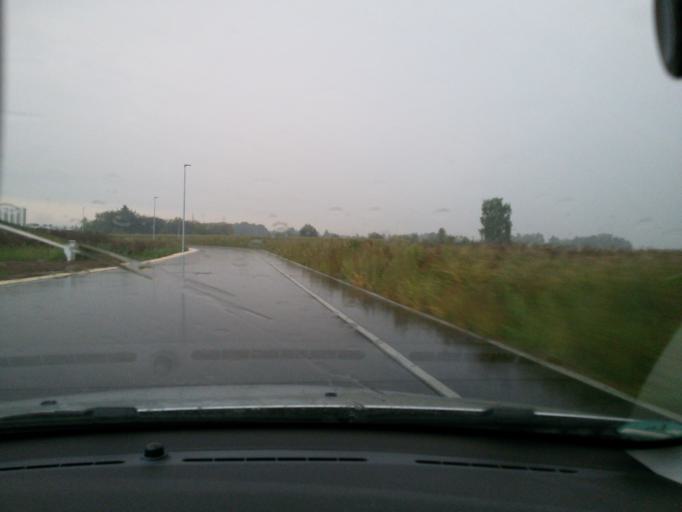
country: DE
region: Bavaria
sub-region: Swabia
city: Langerringen
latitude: 48.1636
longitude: 10.7594
